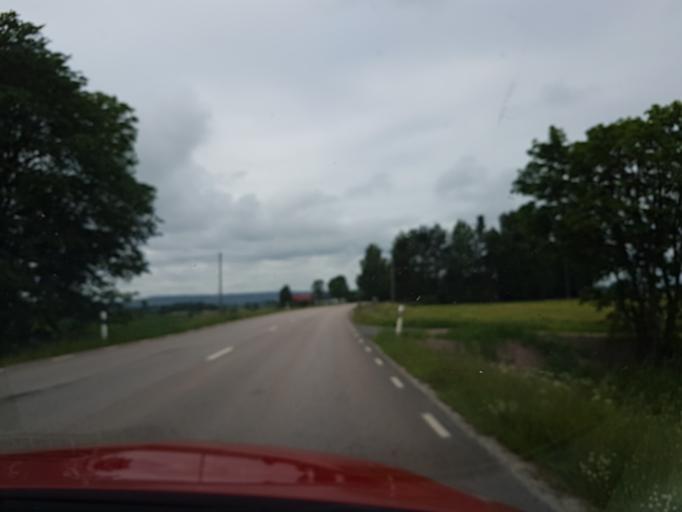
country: SE
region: Vaestra Goetaland
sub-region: Skovde Kommun
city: Skoevde
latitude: 58.3835
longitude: 13.9478
